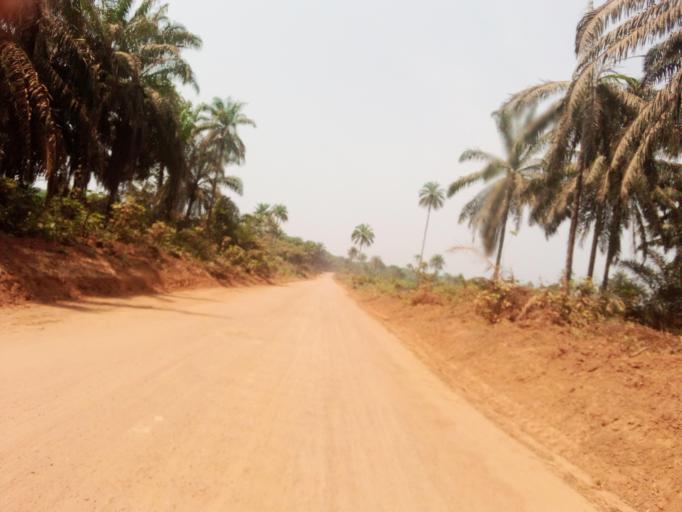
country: SL
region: Southern Province
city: Sumbuya
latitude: 7.6198
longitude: -12.1164
